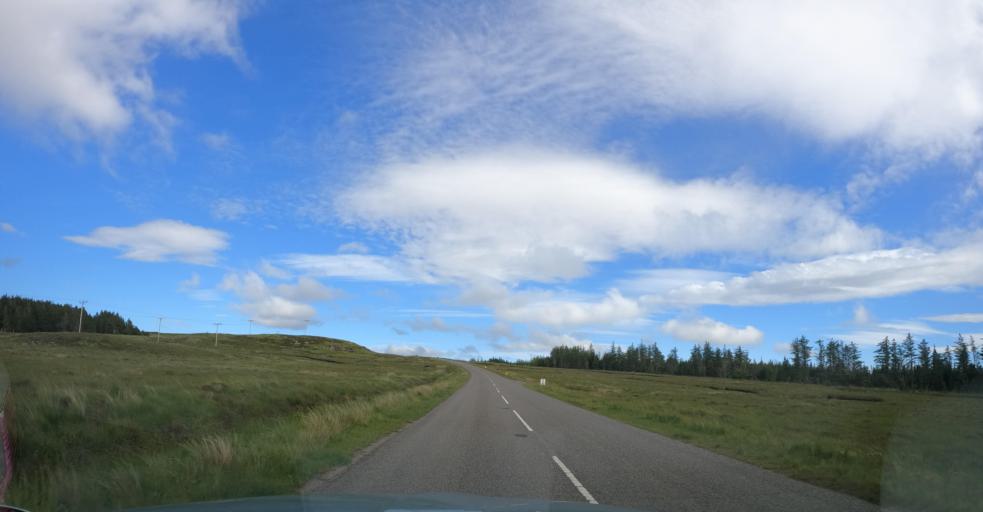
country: GB
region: Scotland
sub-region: Eilean Siar
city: Isle of Lewis
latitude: 58.1811
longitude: -6.6625
